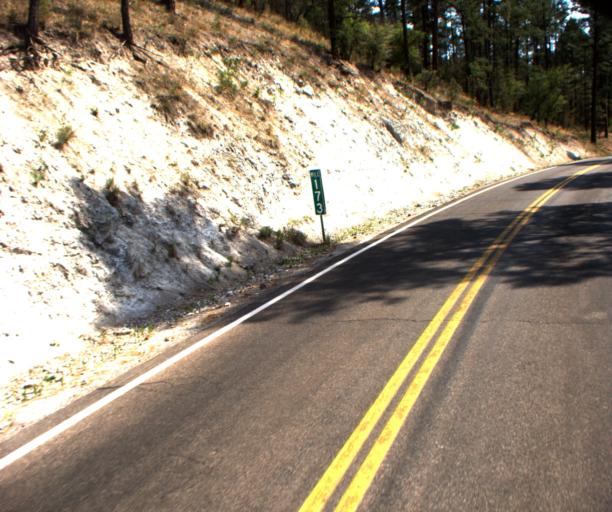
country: US
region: Arizona
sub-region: Greenlee County
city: Clifton
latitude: 33.1010
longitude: -109.0680
